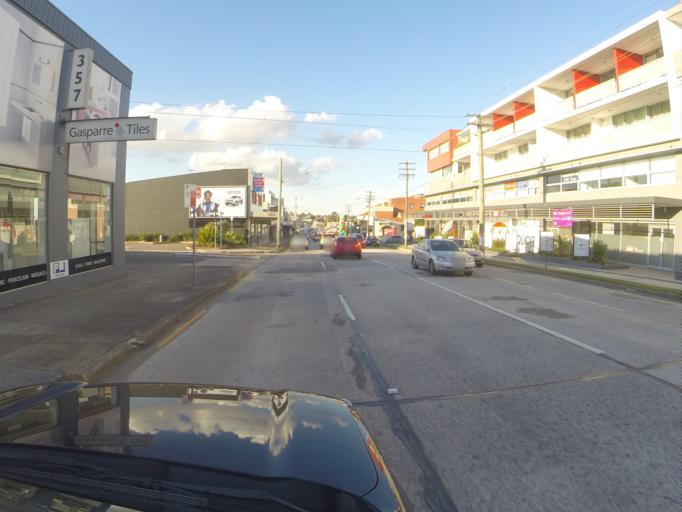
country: AU
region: New South Wales
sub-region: Canterbury
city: Canterbury
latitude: -33.9155
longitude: 151.1108
